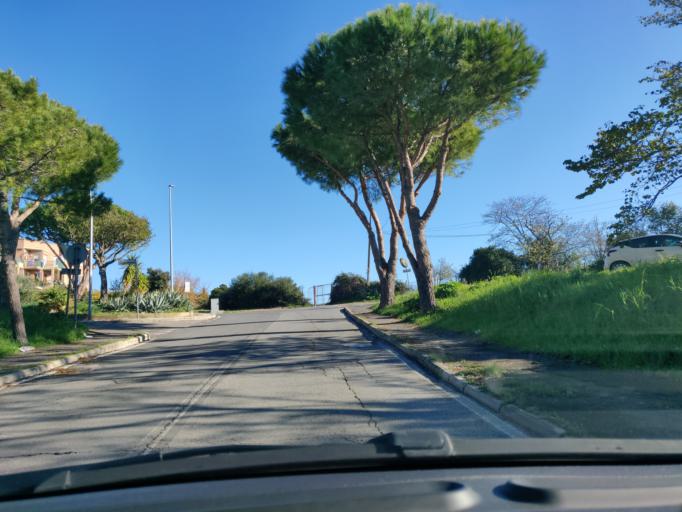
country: IT
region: Latium
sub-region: Citta metropolitana di Roma Capitale
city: Civitavecchia
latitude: 42.0950
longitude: 11.8213
